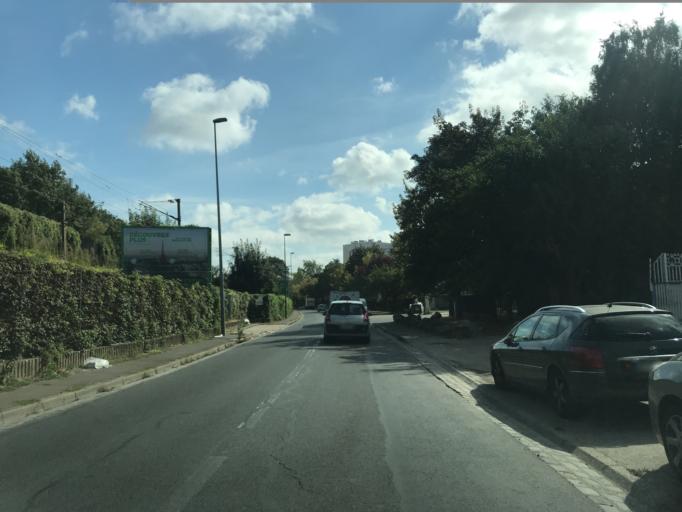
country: FR
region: Ile-de-France
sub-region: Departement de Seine-Saint-Denis
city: Bobigny
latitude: 48.9049
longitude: 2.4363
